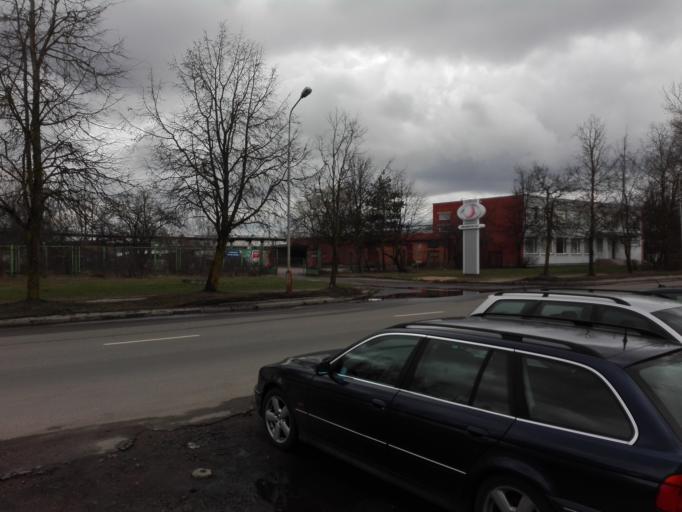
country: LT
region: Vilnius County
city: Vilkpede
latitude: 54.6336
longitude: 25.2653
